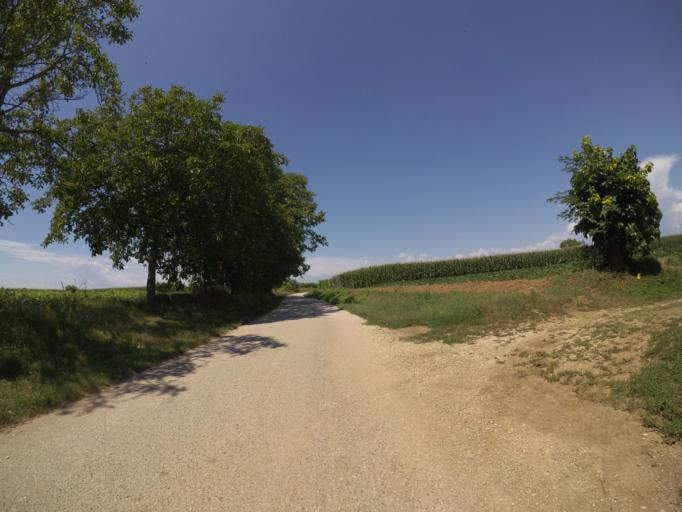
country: IT
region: Friuli Venezia Giulia
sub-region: Provincia di Udine
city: Talmassons
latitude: 45.9356
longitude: 13.1091
